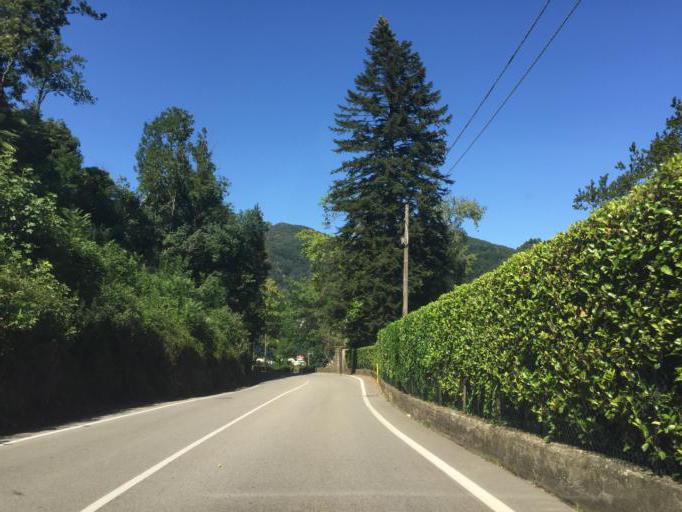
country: IT
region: Lombardy
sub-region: Provincia di Varese
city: Porto Ceresio
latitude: 45.9153
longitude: 8.8984
